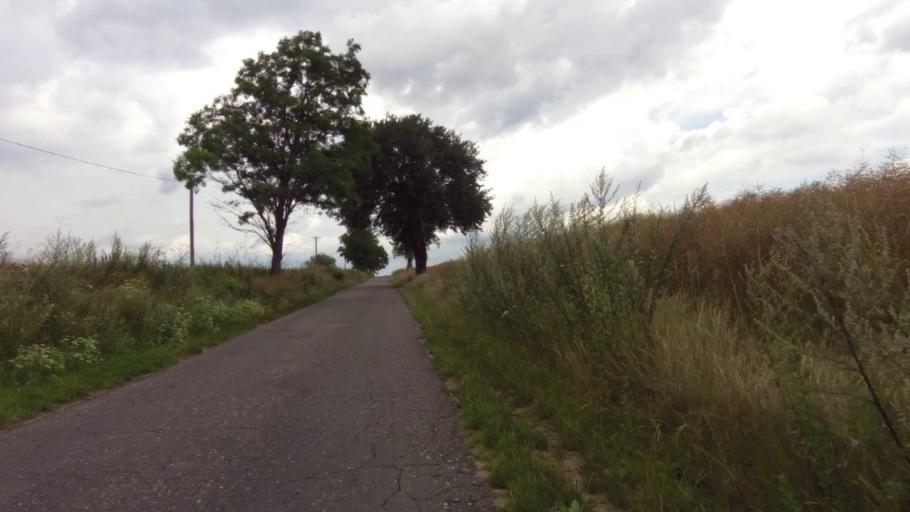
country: PL
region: West Pomeranian Voivodeship
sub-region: Powiat gryfinski
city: Moryn
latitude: 52.8806
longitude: 14.3966
